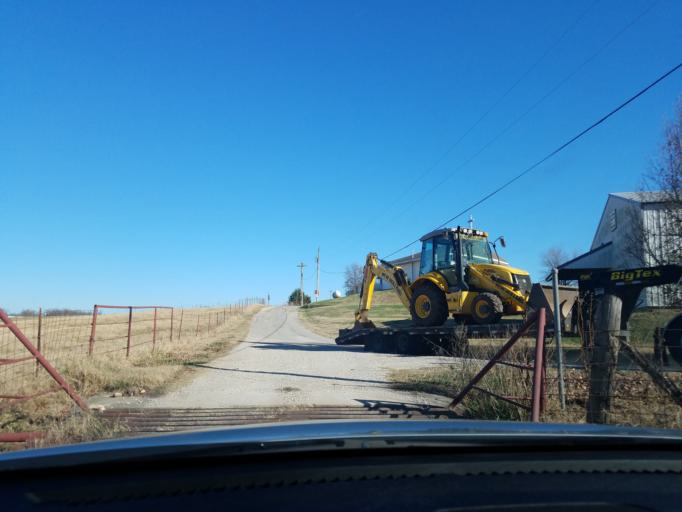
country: US
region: Arkansas
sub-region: Carroll County
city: Berryville
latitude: 36.3856
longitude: -93.6228
